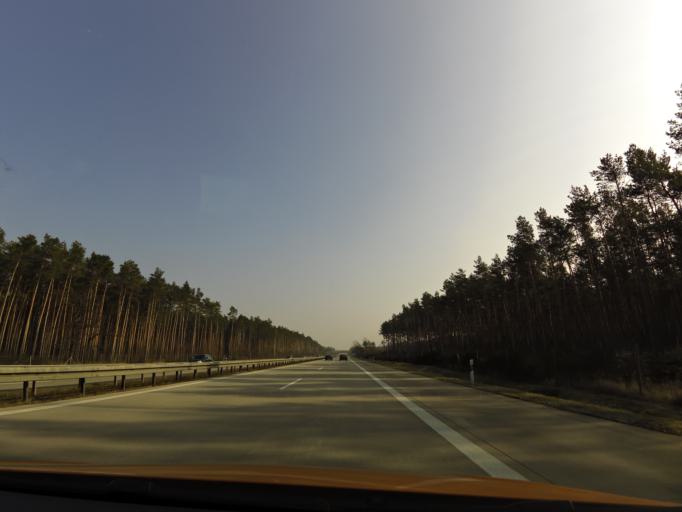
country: DE
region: Brandenburg
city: Briesen
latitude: 52.3237
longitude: 14.3027
